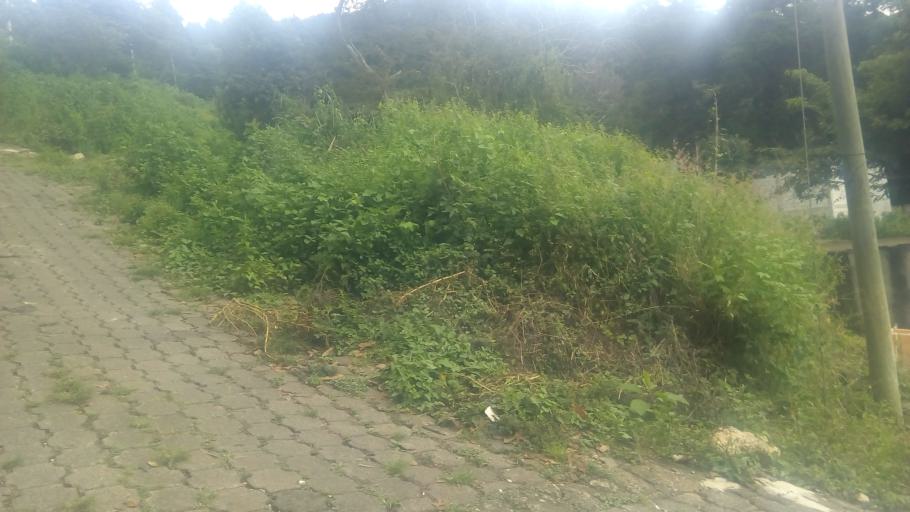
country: GT
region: Guatemala
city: Villa Canales
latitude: 14.5081
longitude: -90.5167
